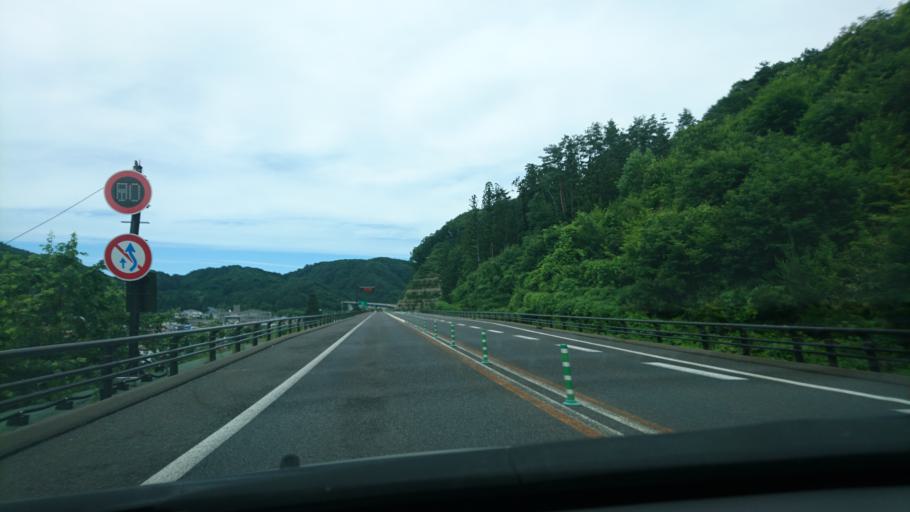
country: JP
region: Iwate
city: Miyako
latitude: 39.9982
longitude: 141.8853
